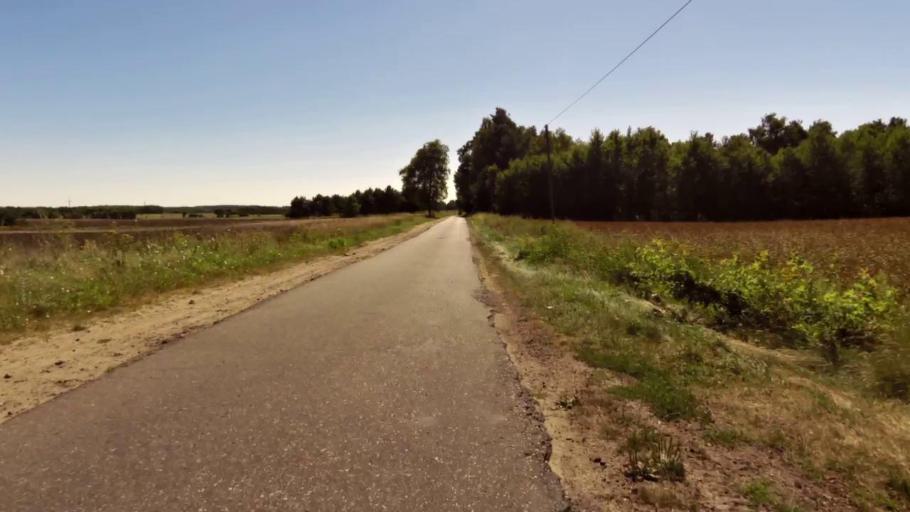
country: PL
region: West Pomeranian Voivodeship
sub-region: Powiat szczecinecki
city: Szczecinek
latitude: 53.6960
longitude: 16.6068
